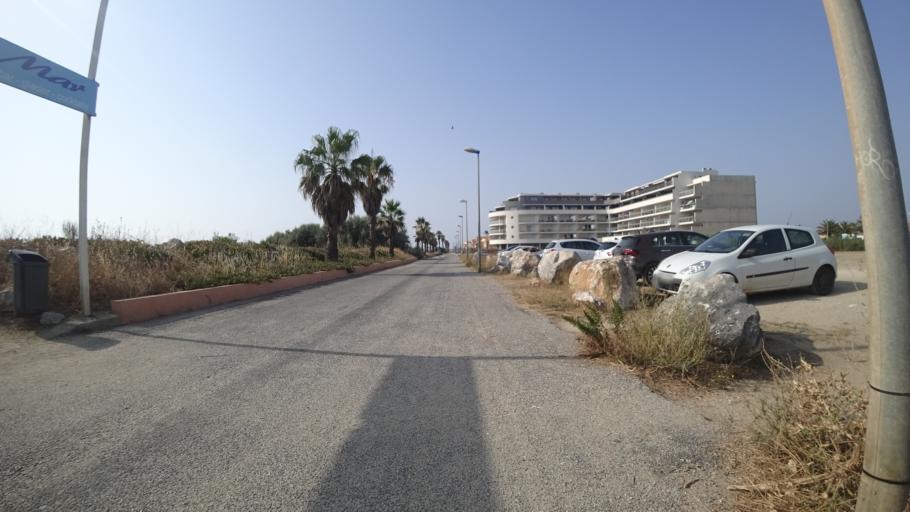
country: FR
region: Languedoc-Roussillon
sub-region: Departement des Pyrenees-Orientales
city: Sainte-Marie-Plage
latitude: 42.7383
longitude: 3.0366
